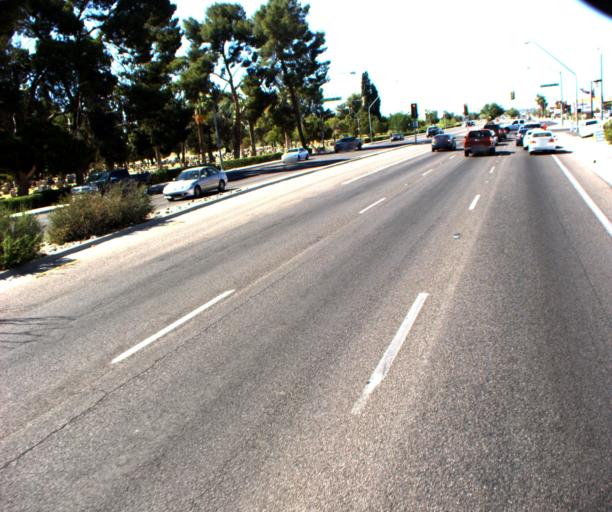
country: US
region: Arizona
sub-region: Pima County
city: Flowing Wells
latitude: 32.2638
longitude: -110.9780
